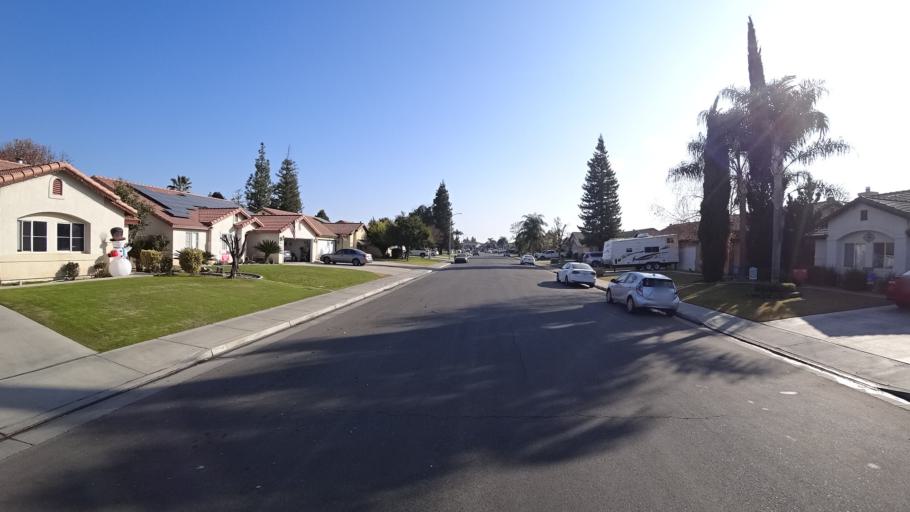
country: US
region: California
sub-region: Kern County
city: Greenacres
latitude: 35.3628
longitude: -119.1132
